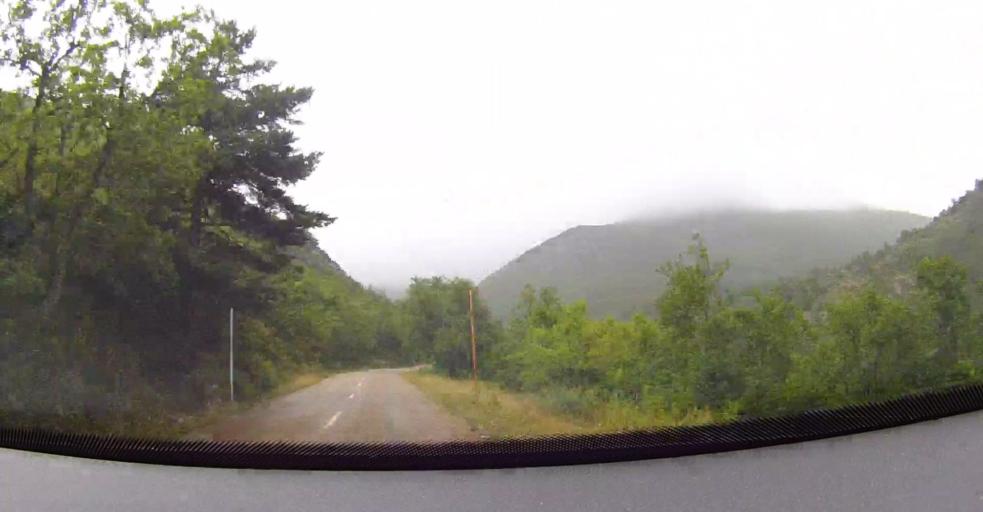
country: ES
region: Castille and Leon
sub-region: Provincia de Leon
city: Puebla de Lillo
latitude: 43.0692
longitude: -5.2657
